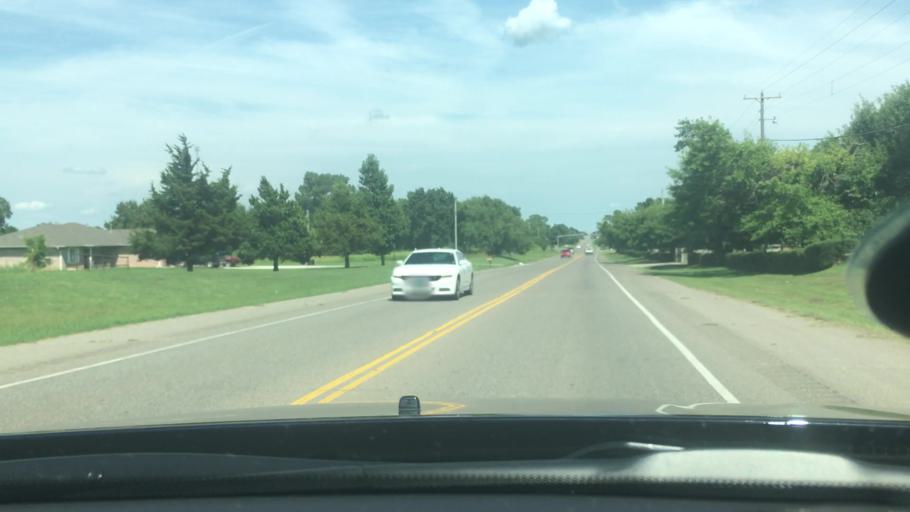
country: US
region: Oklahoma
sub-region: Pottawatomie County
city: Shawnee
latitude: 35.3331
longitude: -96.8641
